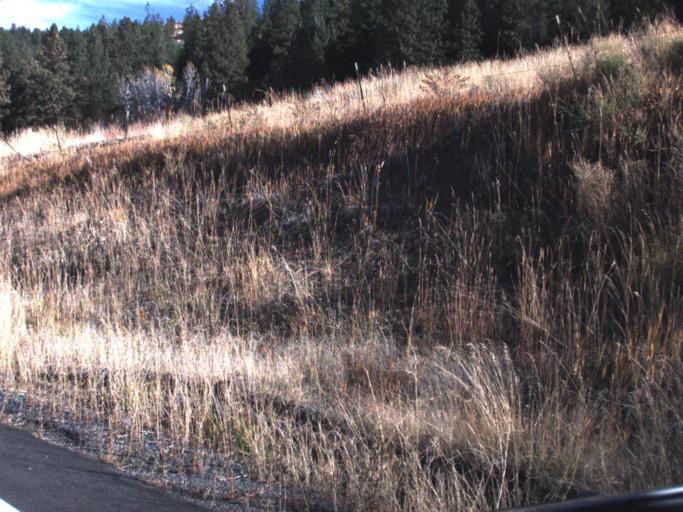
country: US
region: Washington
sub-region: Stevens County
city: Kettle Falls
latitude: 48.1425
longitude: -118.1864
